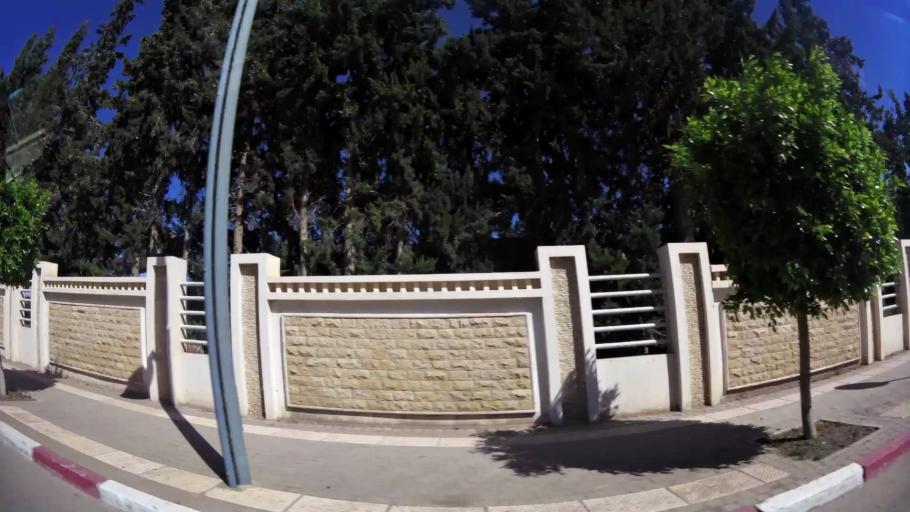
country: MA
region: Oriental
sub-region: Oujda-Angad
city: Oujda
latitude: 34.7180
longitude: -1.9201
